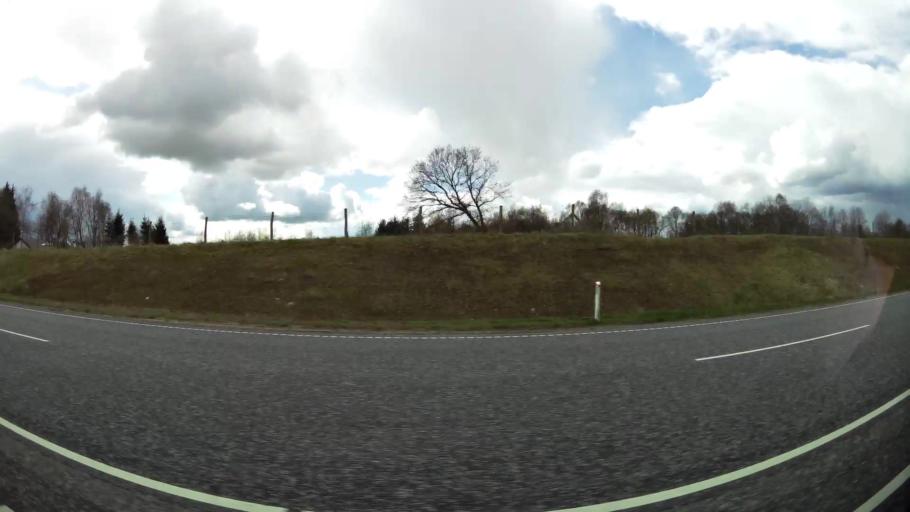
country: DK
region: South Denmark
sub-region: Vejle Kommune
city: Egtved
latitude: 55.7037
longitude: 9.2930
